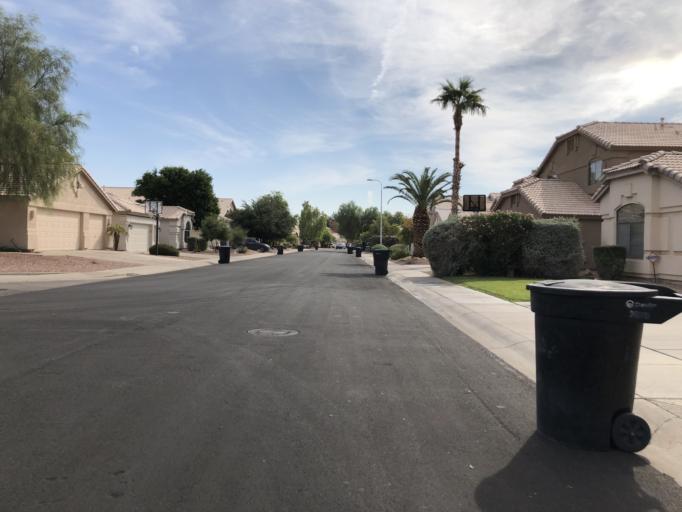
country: US
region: Arizona
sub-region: Maricopa County
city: Guadalupe
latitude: 33.3187
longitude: -111.9183
